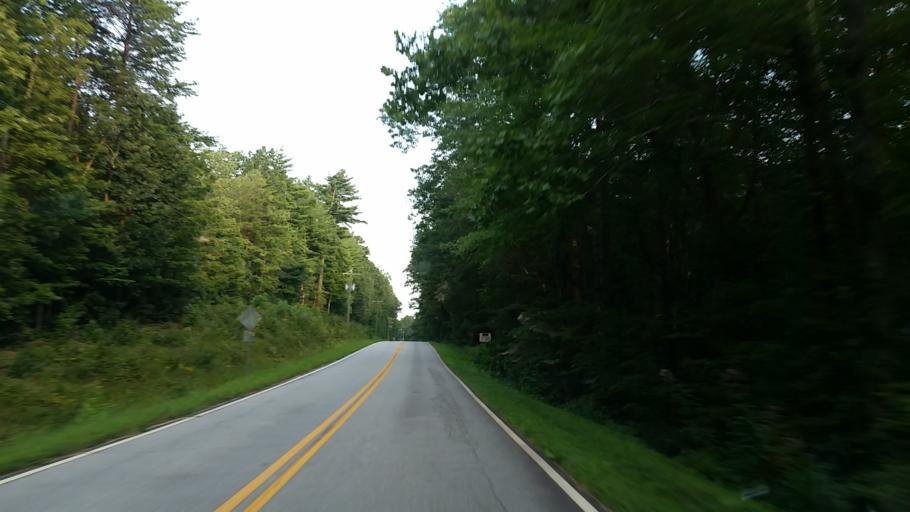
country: US
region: Georgia
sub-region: Lumpkin County
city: Dahlonega
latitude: 34.5969
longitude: -84.0431
